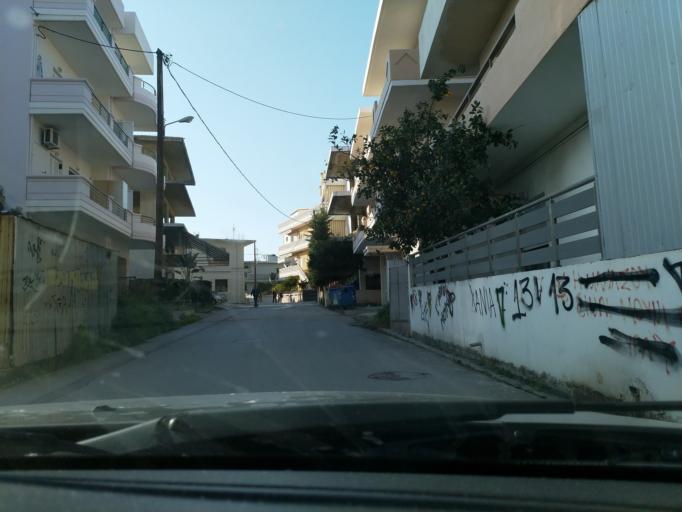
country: GR
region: Crete
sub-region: Nomos Chanias
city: Chania
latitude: 35.5007
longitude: 24.0247
